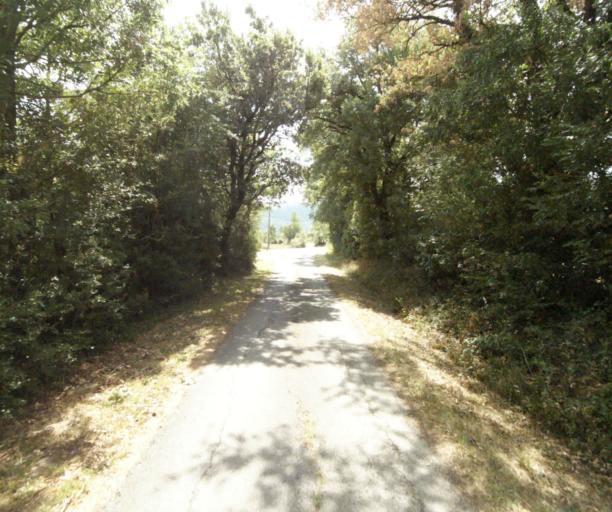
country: FR
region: Midi-Pyrenees
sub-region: Departement du Tarn
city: Dourgne
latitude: 43.4824
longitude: 2.1140
